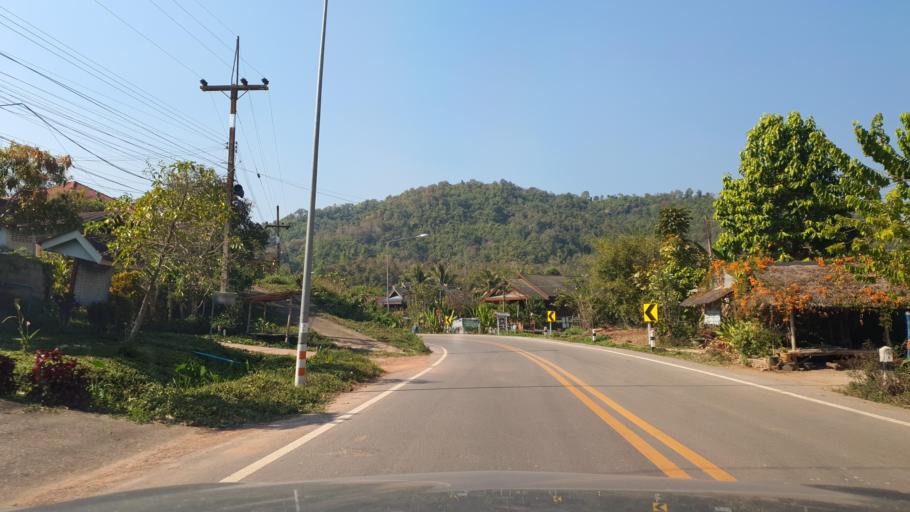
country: TH
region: Chiang Rai
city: Mae Lao
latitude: 19.8378
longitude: 99.6809
